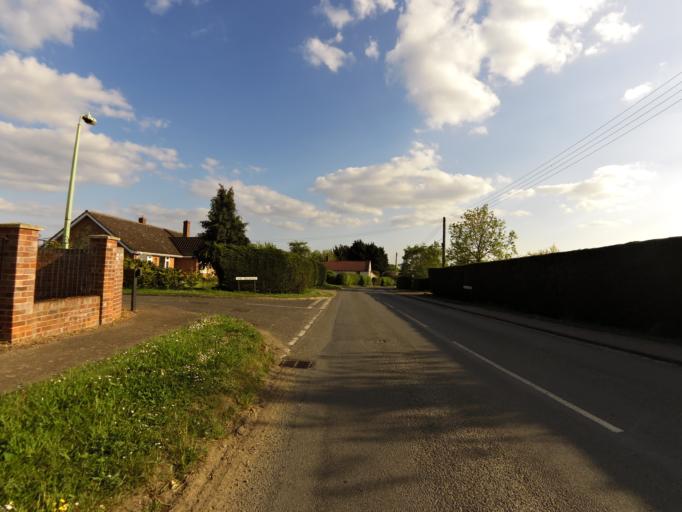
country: GB
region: England
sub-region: Suffolk
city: Beccles
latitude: 52.4042
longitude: 1.5410
